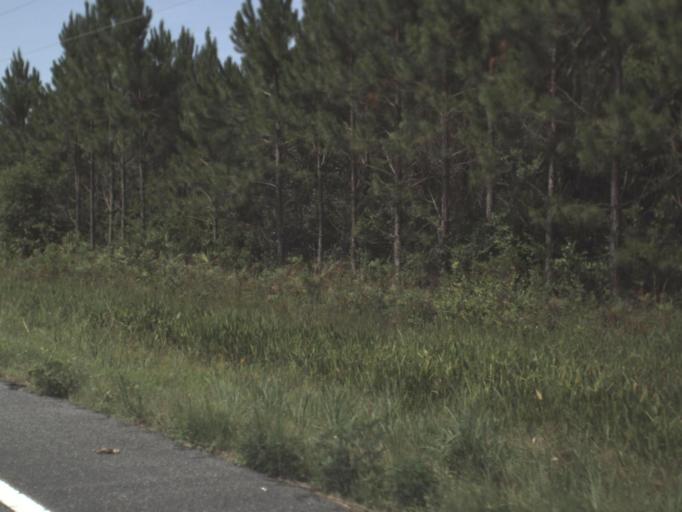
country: US
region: Florida
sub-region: Lafayette County
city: Mayo
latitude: 30.0127
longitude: -83.1934
